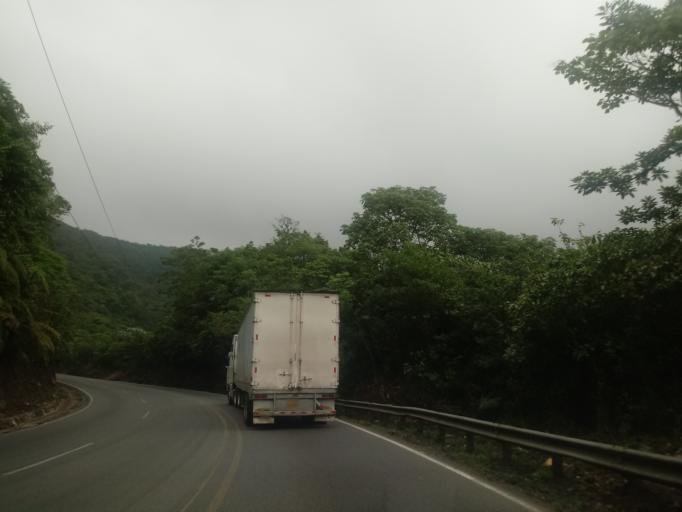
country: CR
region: Heredia
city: Angeles
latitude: 10.0562
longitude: -84.0081
